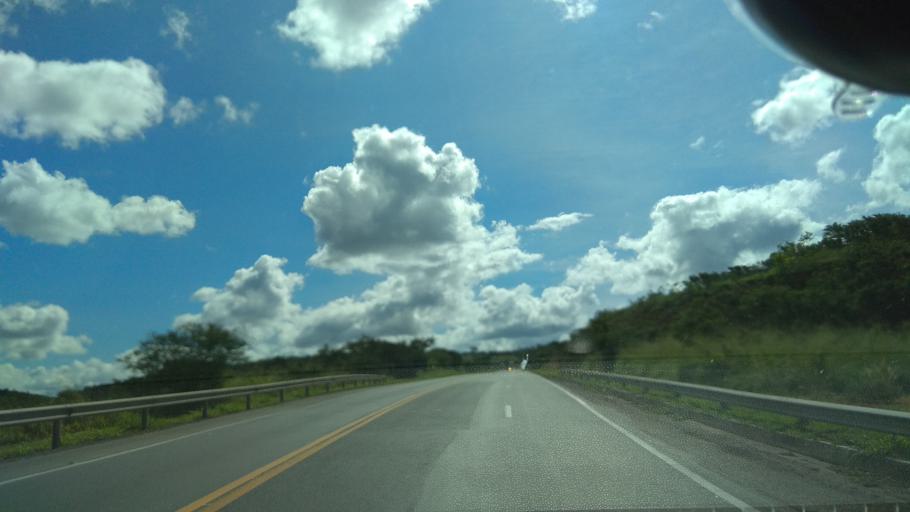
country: BR
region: Bahia
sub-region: Santa Ines
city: Santa Ines
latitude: -13.2235
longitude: -40.0257
